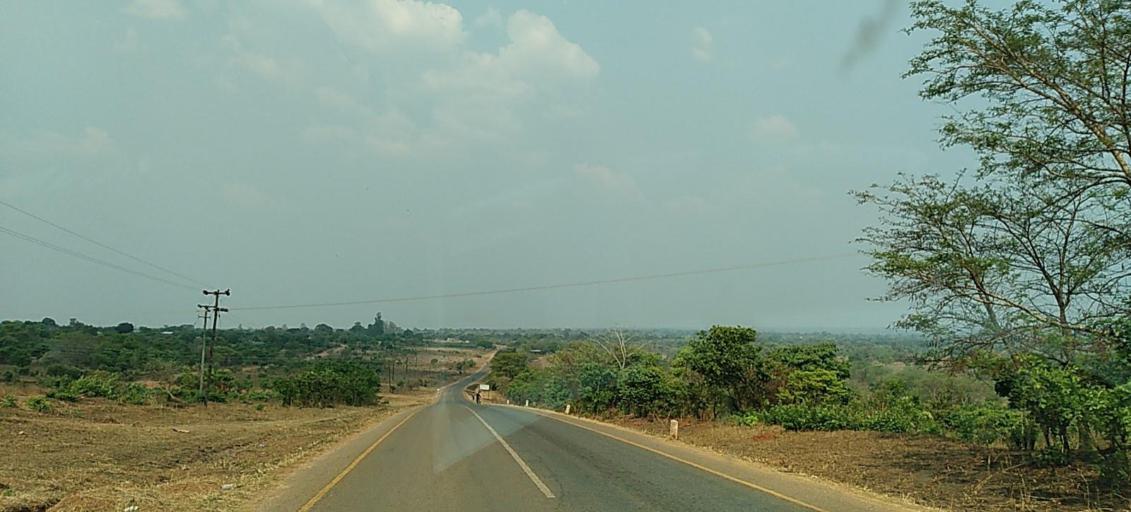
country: ZM
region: North-Western
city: Kabompo
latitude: -13.5916
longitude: 24.2118
